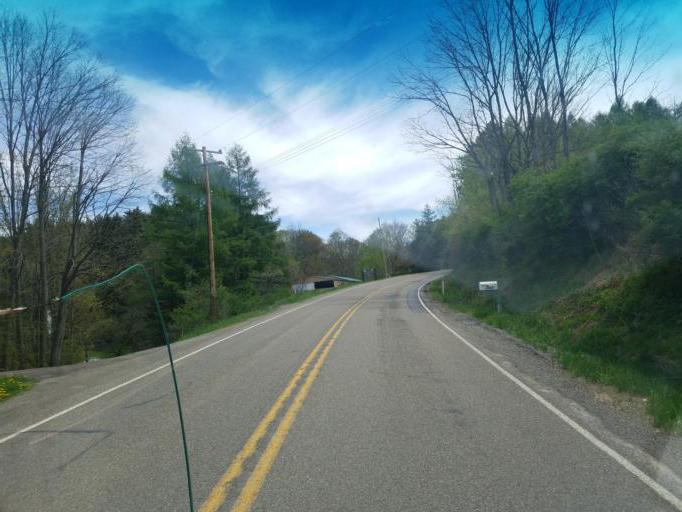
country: US
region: Pennsylvania
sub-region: Tioga County
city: Wellsboro
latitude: 41.7301
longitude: -77.4106
